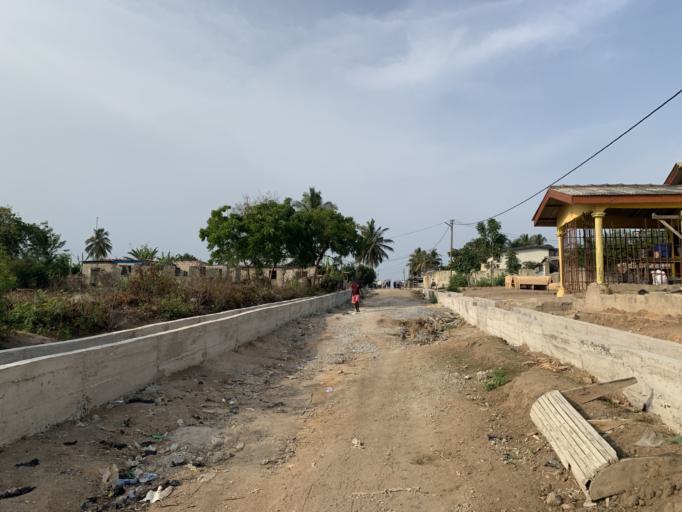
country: GH
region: Central
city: Winneba
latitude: 5.3348
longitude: -0.6243
